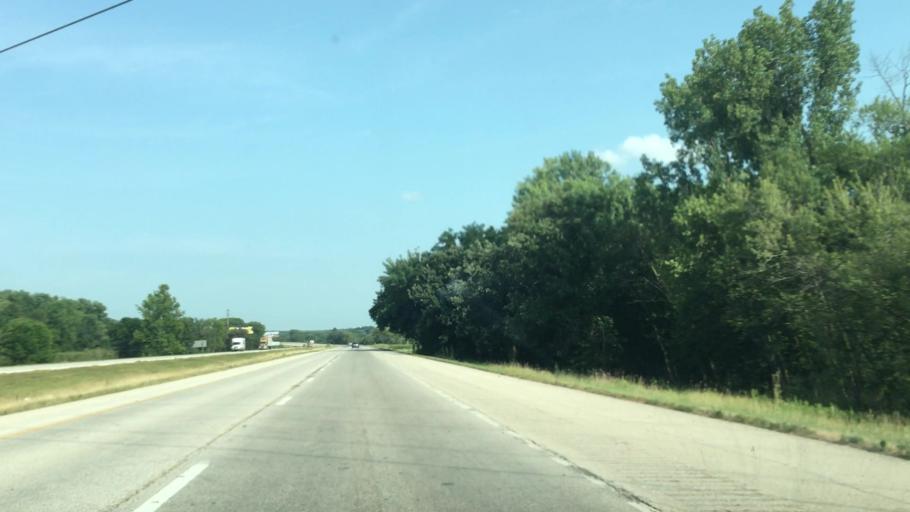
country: US
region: Illinois
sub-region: Rock Island County
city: Milan
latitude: 41.4512
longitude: -90.5917
